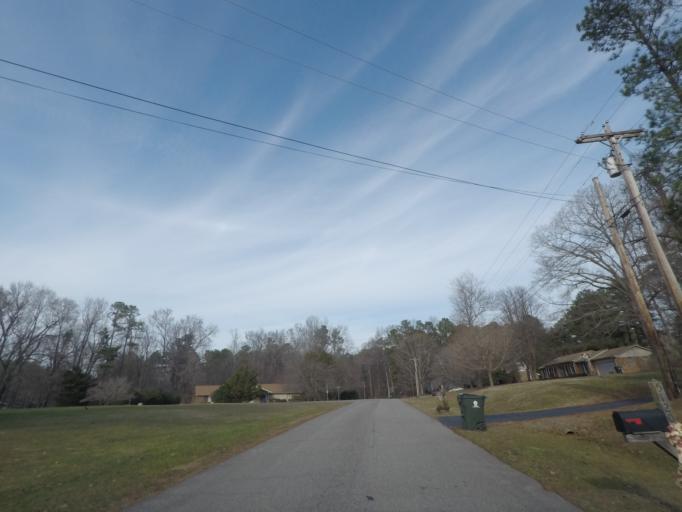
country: US
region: North Carolina
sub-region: Durham County
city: Durham
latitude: 36.0774
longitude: -78.9665
